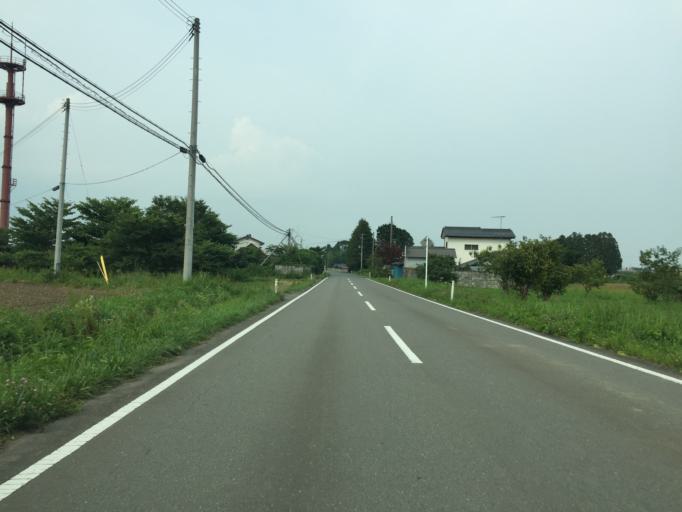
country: JP
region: Fukushima
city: Namie
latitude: 37.6007
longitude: 140.9191
